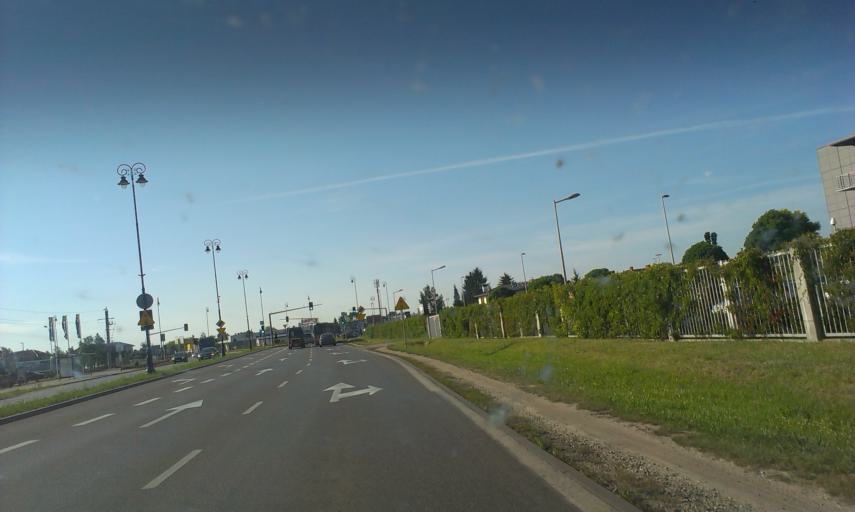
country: PL
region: Masovian Voivodeship
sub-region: Powiat piaseczynski
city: Konstancin-Jeziorna
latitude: 52.1110
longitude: 21.1117
